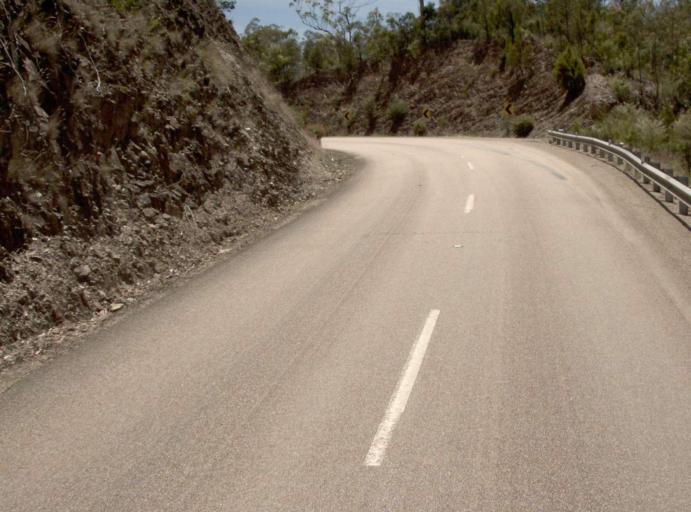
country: AU
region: Victoria
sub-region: East Gippsland
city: Bairnsdale
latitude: -37.4514
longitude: 147.8285
